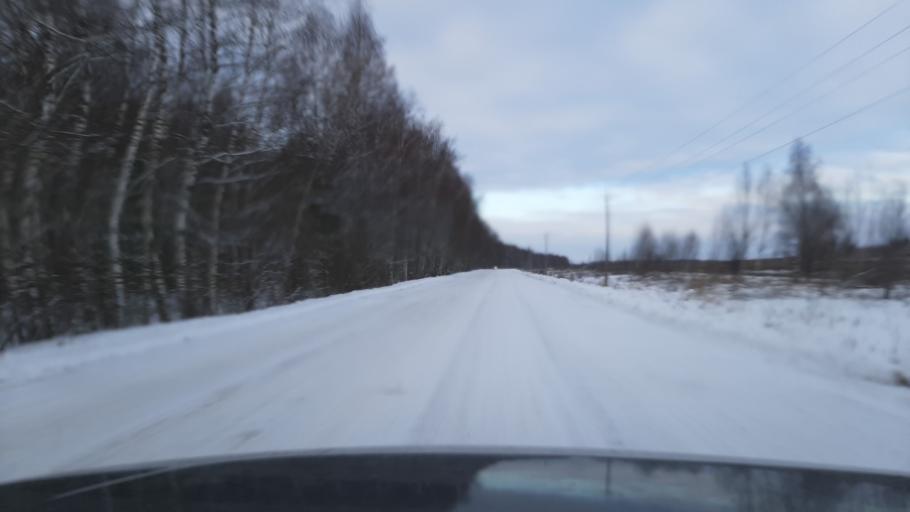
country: RU
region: Kostroma
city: Nerekhta
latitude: 57.4704
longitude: 40.6876
